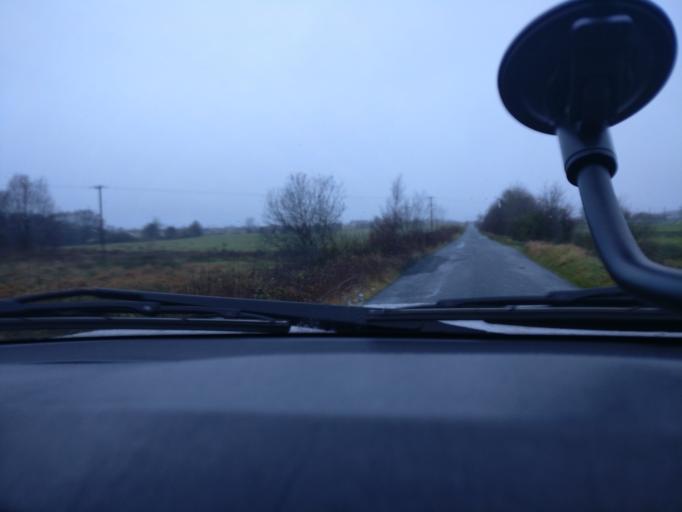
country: IE
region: Connaught
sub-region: County Galway
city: Loughrea
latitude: 53.2359
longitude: -8.5235
